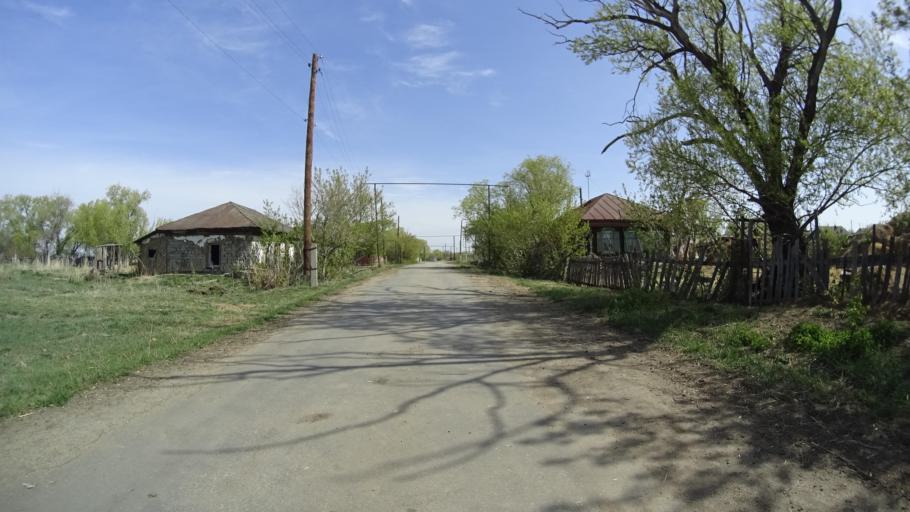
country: RU
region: Chelyabinsk
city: Chesma
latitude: 53.8003
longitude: 61.0172
